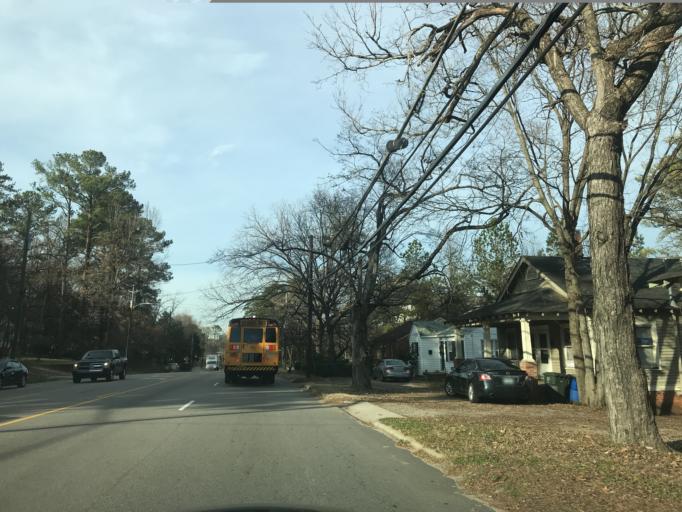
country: US
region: North Carolina
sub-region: Wake County
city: Raleigh
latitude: 35.8083
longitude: -78.6249
